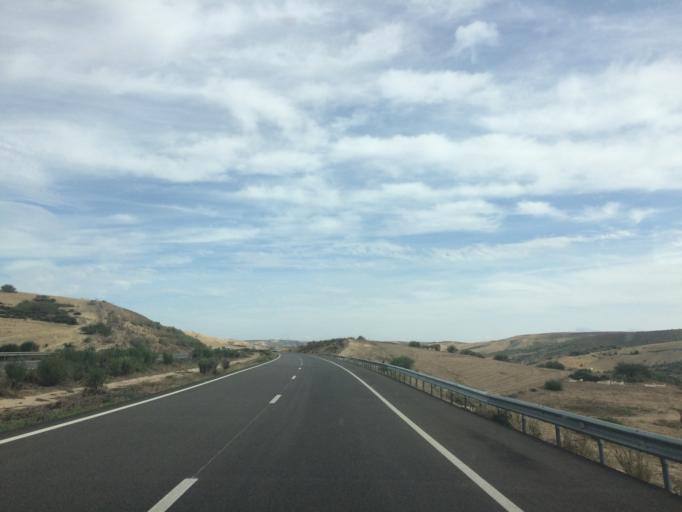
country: MA
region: Rabat-Sale-Zemmour-Zaer
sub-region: Khemisset
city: Khemisset
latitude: 33.8389
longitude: -5.8304
